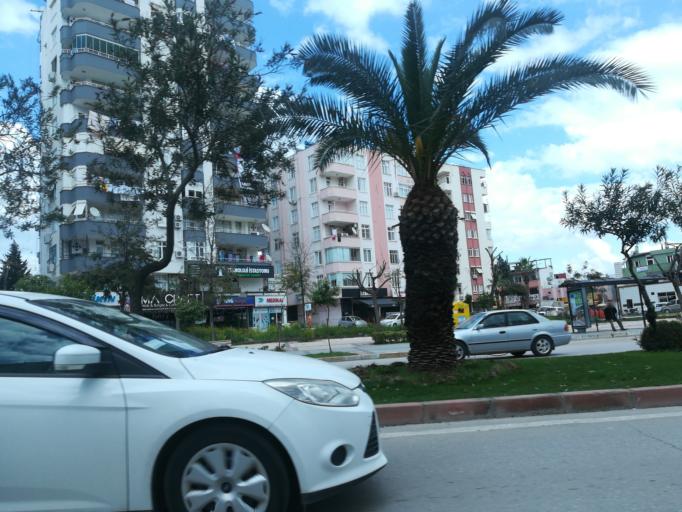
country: TR
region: Adana
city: Adana
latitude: 37.0421
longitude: 35.3129
